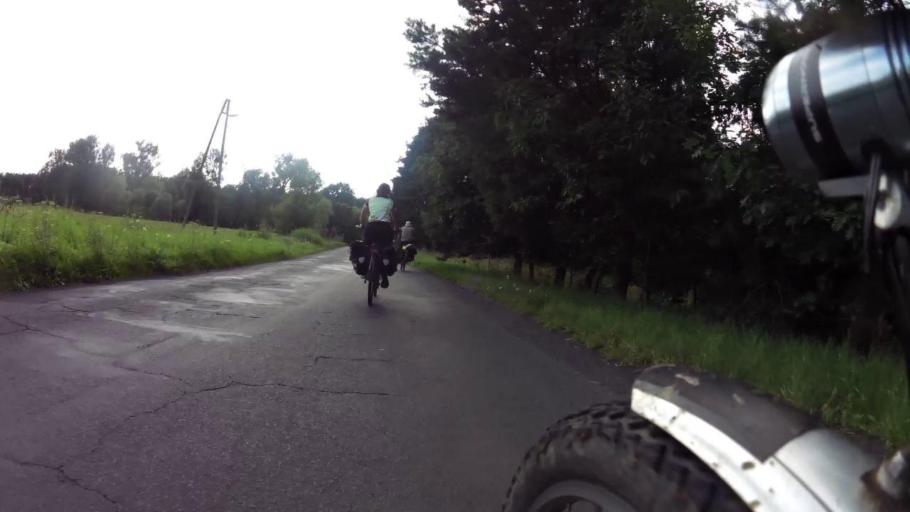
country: PL
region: West Pomeranian Voivodeship
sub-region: Powiat gryfinski
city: Gryfino
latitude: 53.2307
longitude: 14.5506
